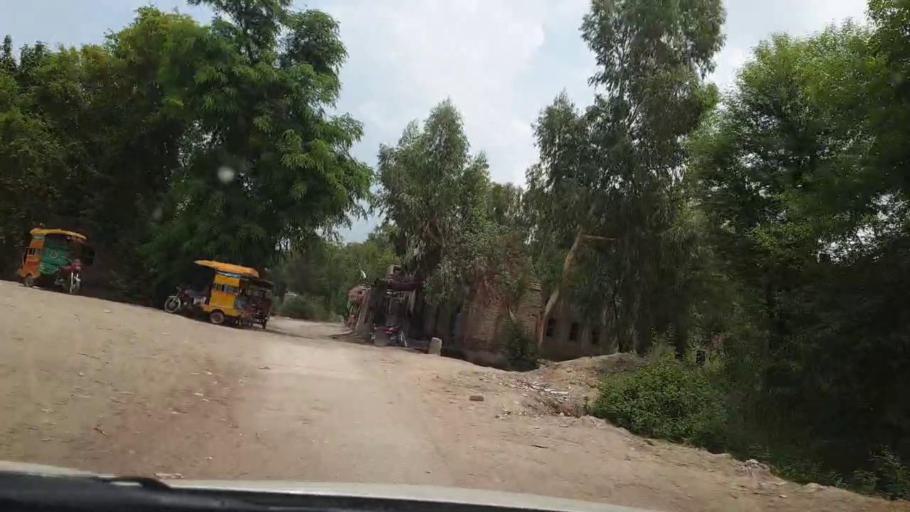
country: PK
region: Sindh
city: Dokri
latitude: 27.3965
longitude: 68.1094
